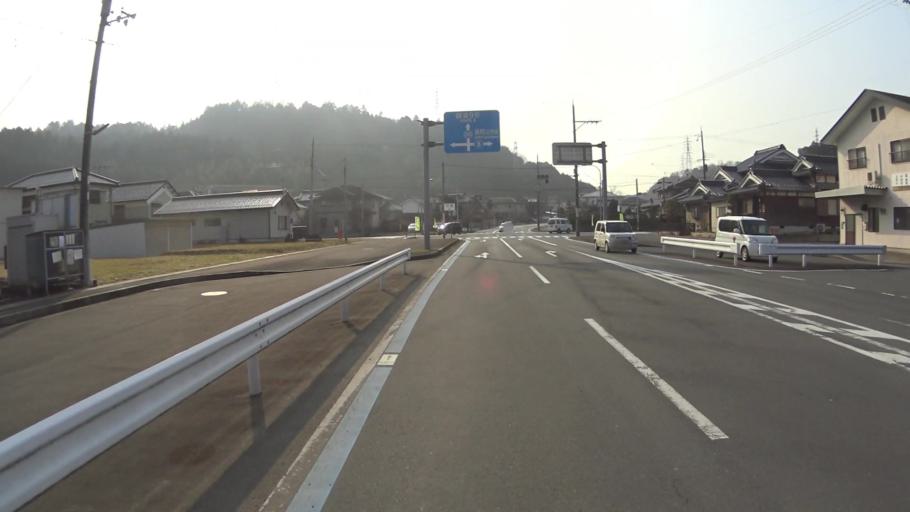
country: JP
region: Kyoto
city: Fukuchiyama
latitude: 35.2997
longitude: 135.1796
